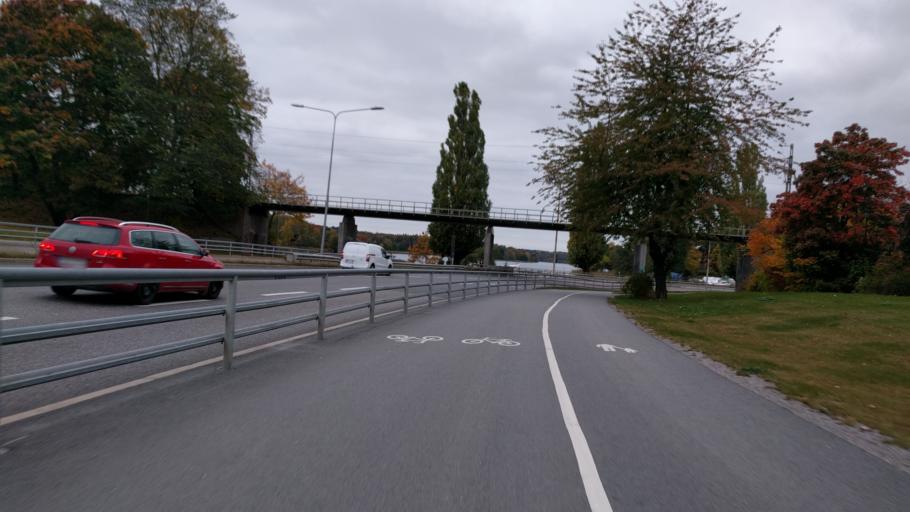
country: SE
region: Stockholm
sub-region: Stockholms Kommun
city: Stockholm
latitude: 59.3532
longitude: 18.0538
